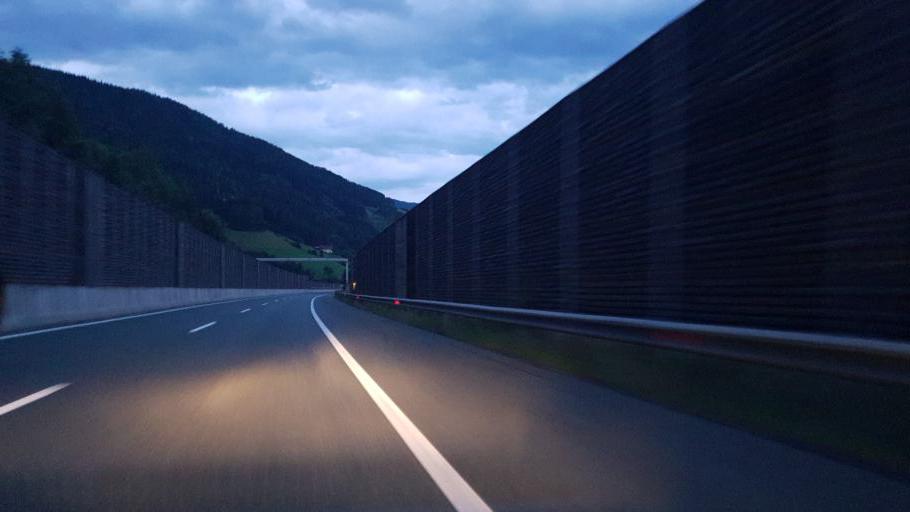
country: AT
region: Carinthia
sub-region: Politischer Bezirk Spittal an der Drau
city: Gmuend
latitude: 46.9404
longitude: 13.6089
